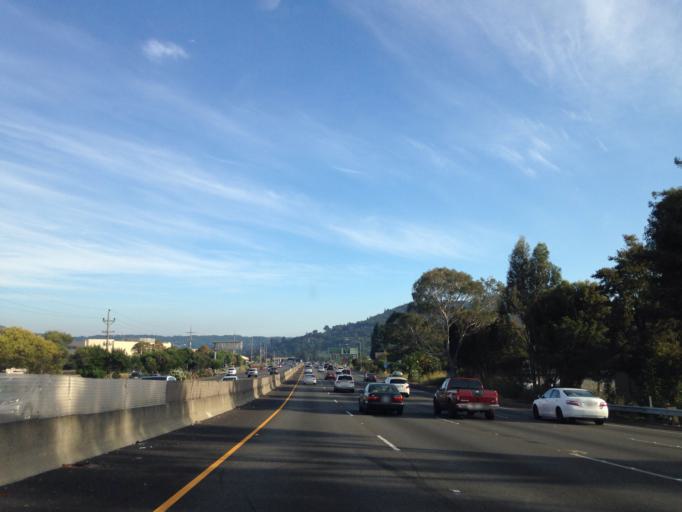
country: US
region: California
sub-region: Marin County
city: Corte Madera
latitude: 37.9338
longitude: -122.5165
